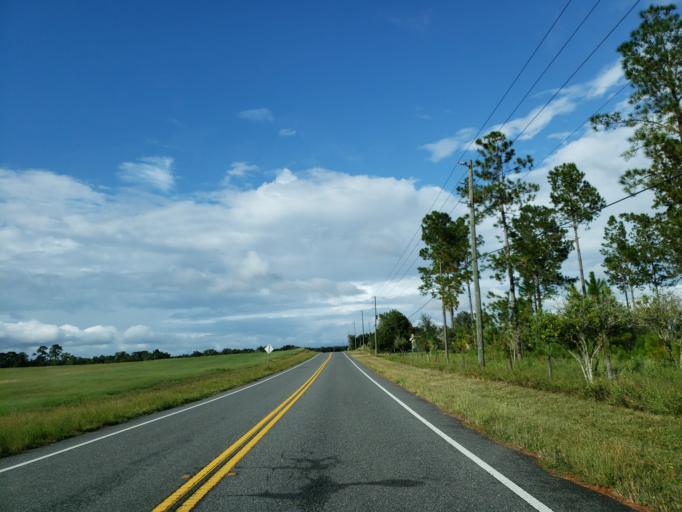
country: US
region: Florida
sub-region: Hernando County
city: Hill 'n Dale
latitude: 28.4598
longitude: -82.3021
